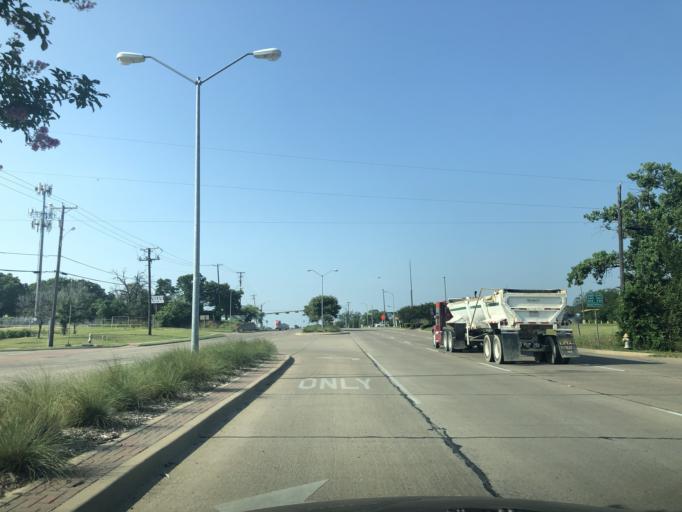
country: US
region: Texas
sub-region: Dallas County
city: Irving
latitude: 32.8073
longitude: -96.9943
